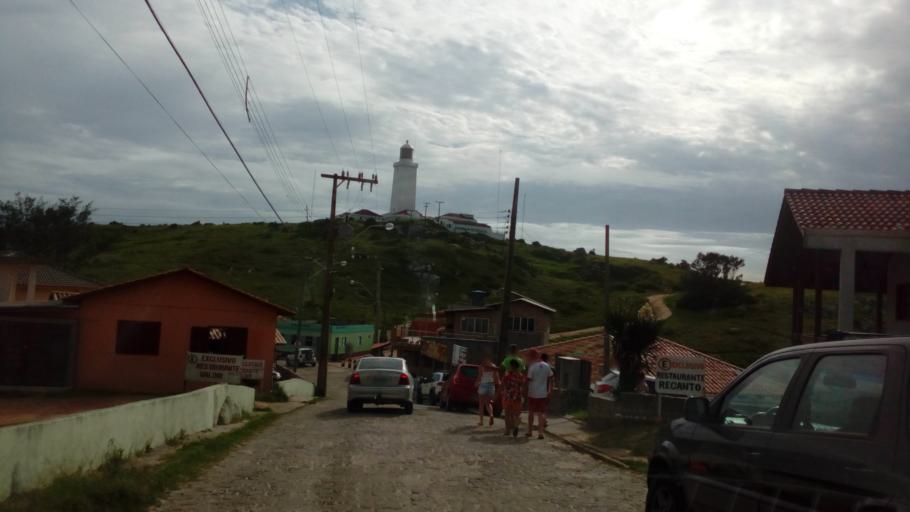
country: BR
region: Santa Catarina
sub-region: Laguna
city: Laguna
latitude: -28.6051
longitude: -48.8165
